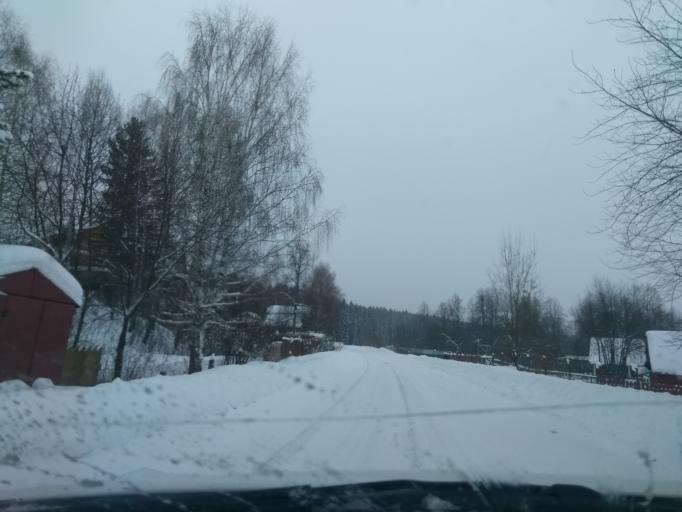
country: RU
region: Perm
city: Sylva
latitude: 57.8430
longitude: 56.7452
